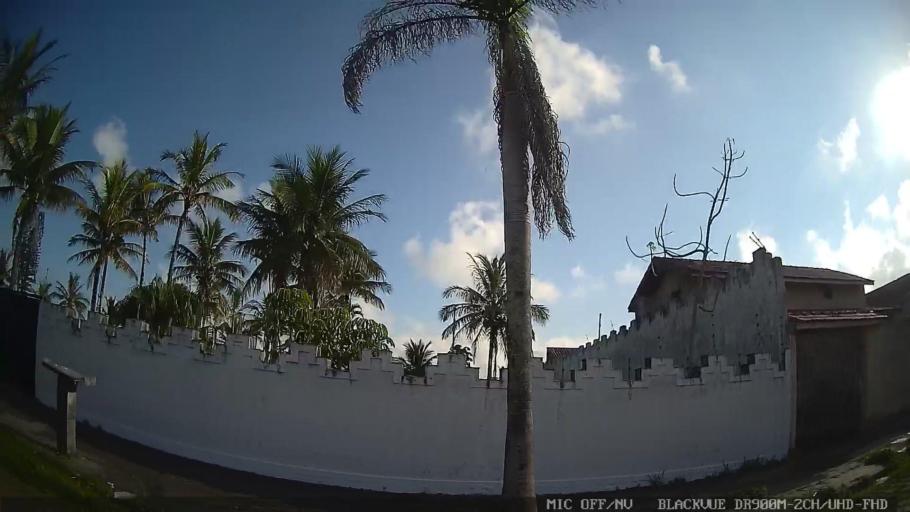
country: BR
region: Sao Paulo
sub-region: Peruibe
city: Peruibe
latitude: -24.2931
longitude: -46.9604
